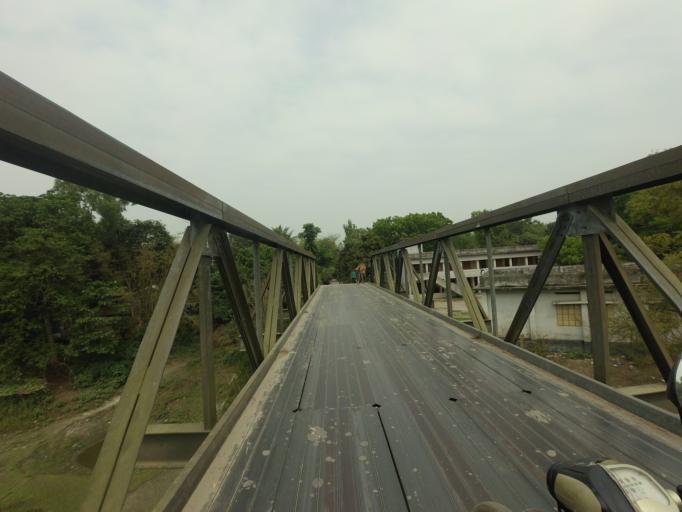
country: BD
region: Rajshahi
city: Sirajganj
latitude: 24.3412
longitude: 89.6826
